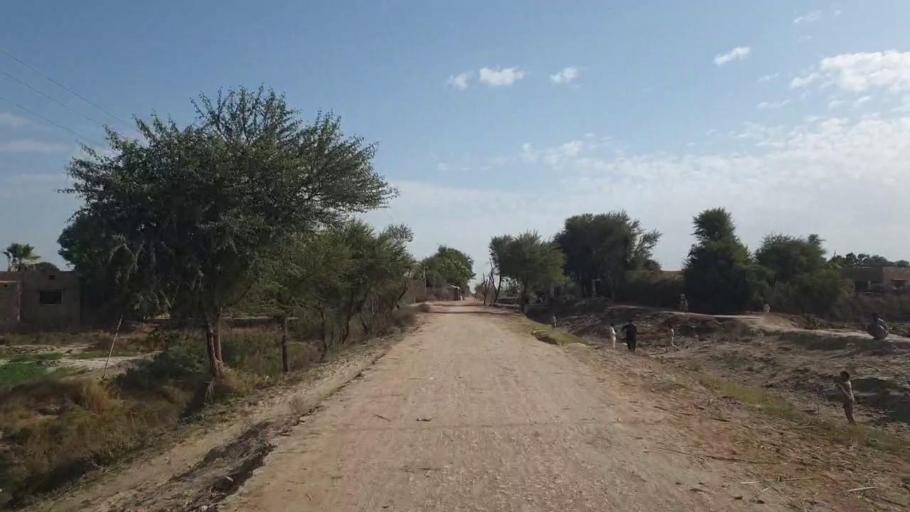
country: PK
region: Sindh
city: Shahdadpur
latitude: 26.0217
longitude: 68.4930
